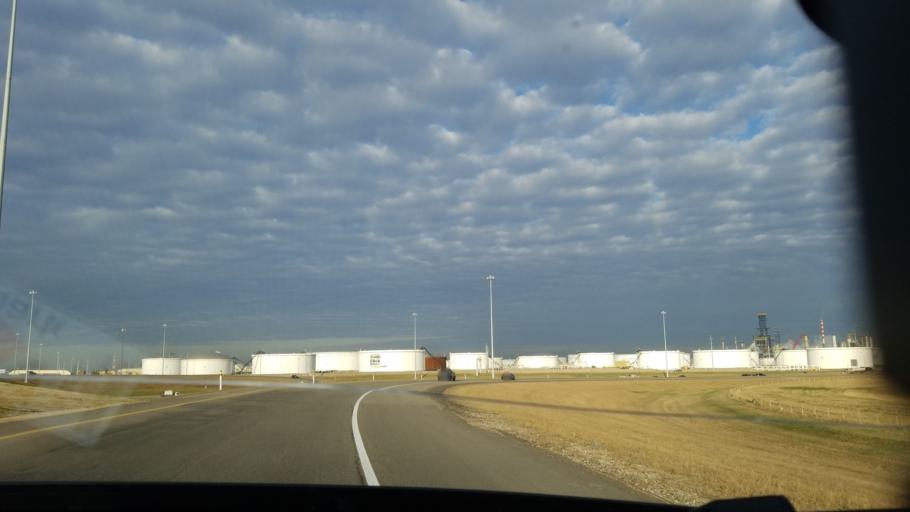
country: CA
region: Alberta
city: Sherwood Park
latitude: 53.5412
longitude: -113.3390
